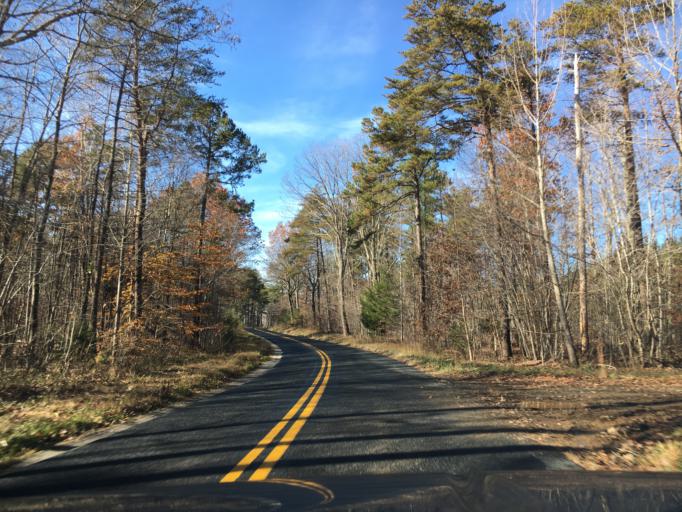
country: US
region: Virginia
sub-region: Buckingham County
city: Buckingham
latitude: 37.4346
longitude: -78.6522
